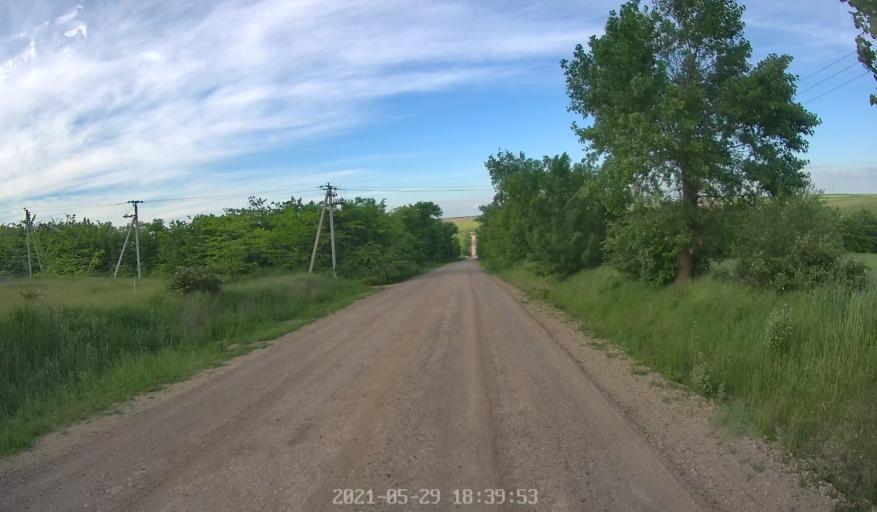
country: MD
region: Chisinau
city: Singera
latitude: 46.8027
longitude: 28.9474
